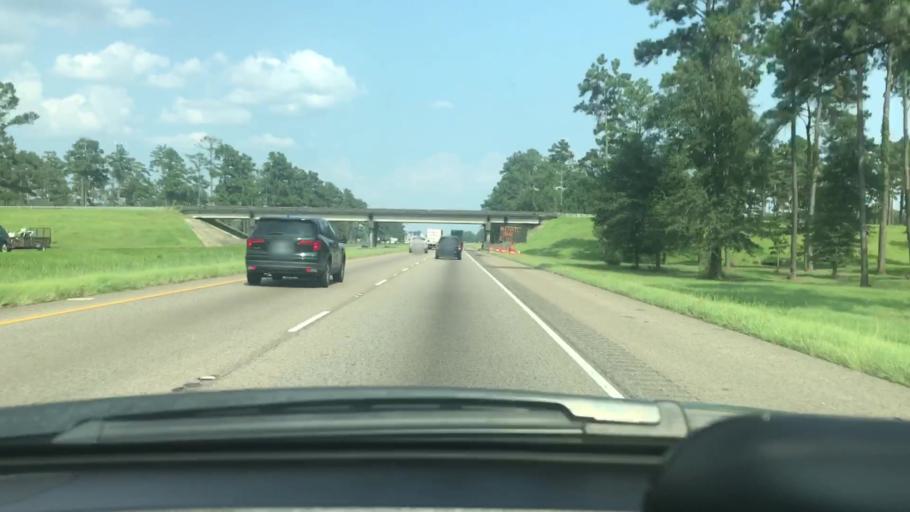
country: US
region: Louisiana
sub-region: Livingston Parish
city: Albany
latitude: 30.4746
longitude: -90.6444
